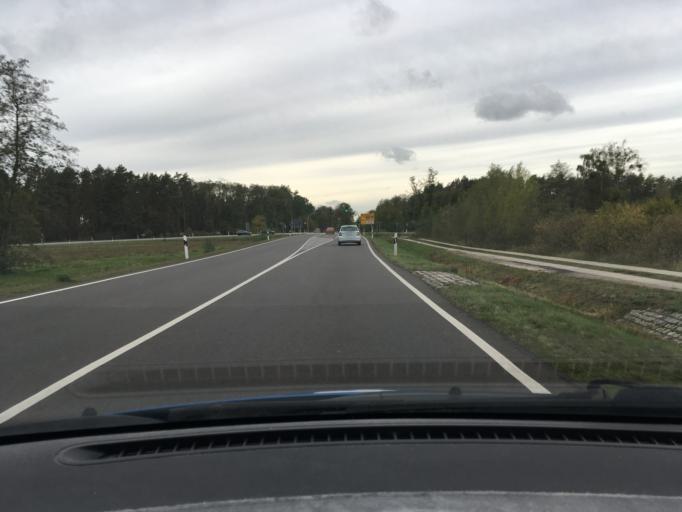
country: DE
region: Saxony-Anhalt
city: Gommern
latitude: 52.0872
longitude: 11.8120
